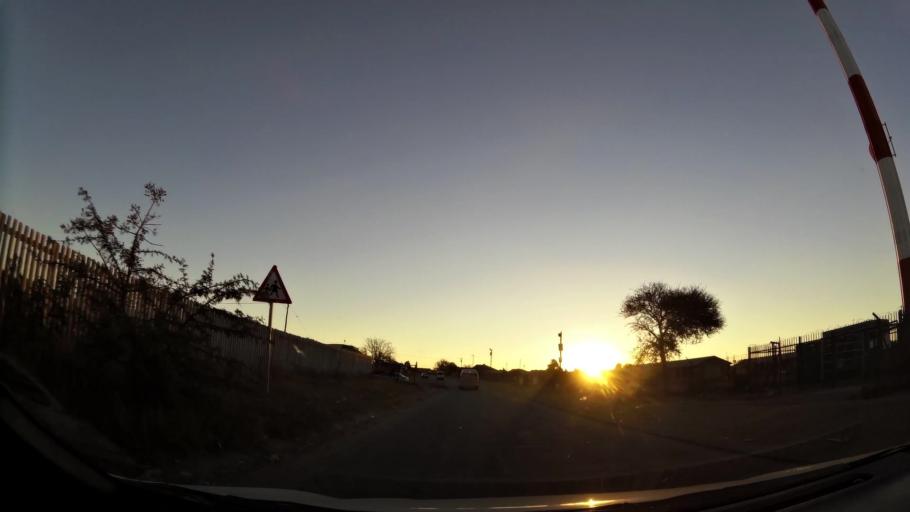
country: ZA
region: Limpopo
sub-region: Capricorn District Municipality
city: Polokwane
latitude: -23.8580
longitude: 29.3680
